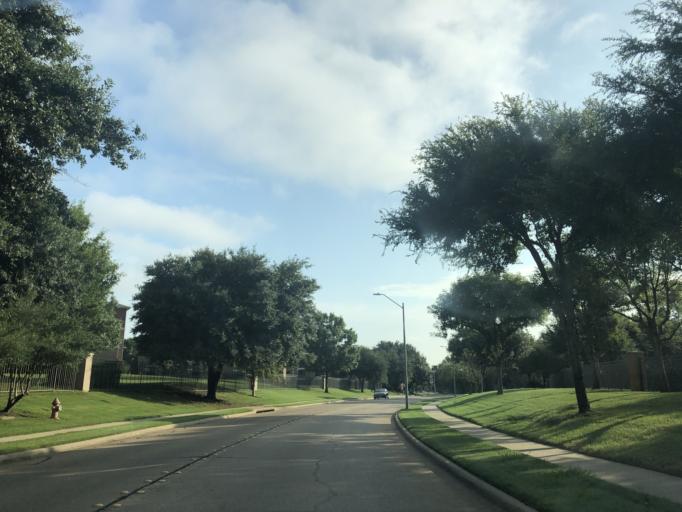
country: US
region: Texas
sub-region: Tarrant County
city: Euless
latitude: 32.8555
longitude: -97.0711
